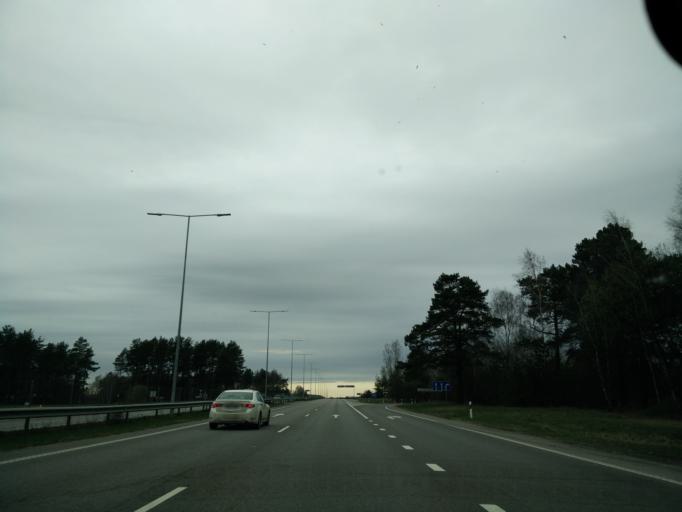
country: LT
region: Vilnius County
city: Lazdynai
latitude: 54.6529
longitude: 25.1554
